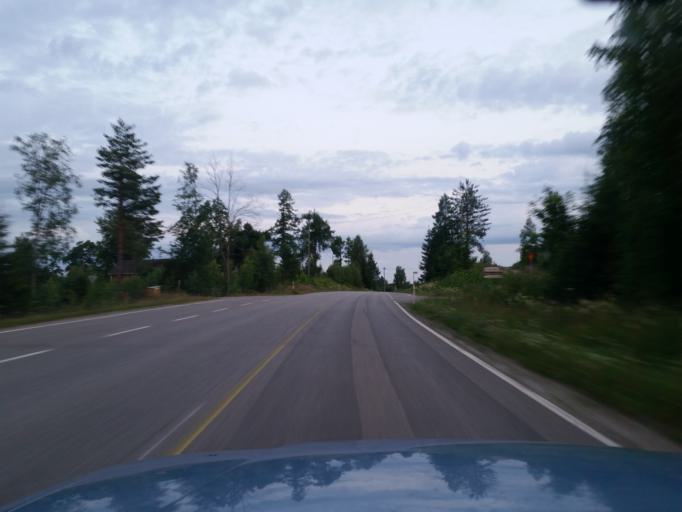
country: FI
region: Southern Savonia
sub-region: Savonlinna
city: Sulkava
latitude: 61.8189
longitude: 28.4372
